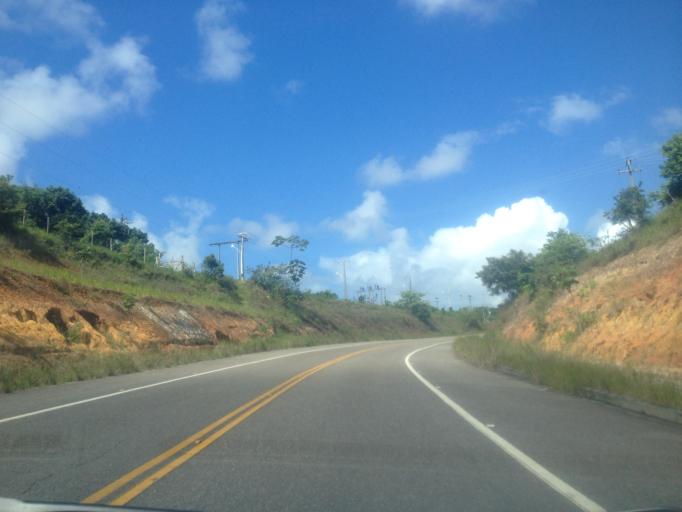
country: BR
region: Sergipe
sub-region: Indiaroba
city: Indiaroba
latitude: -11.4785
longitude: -37.4882
